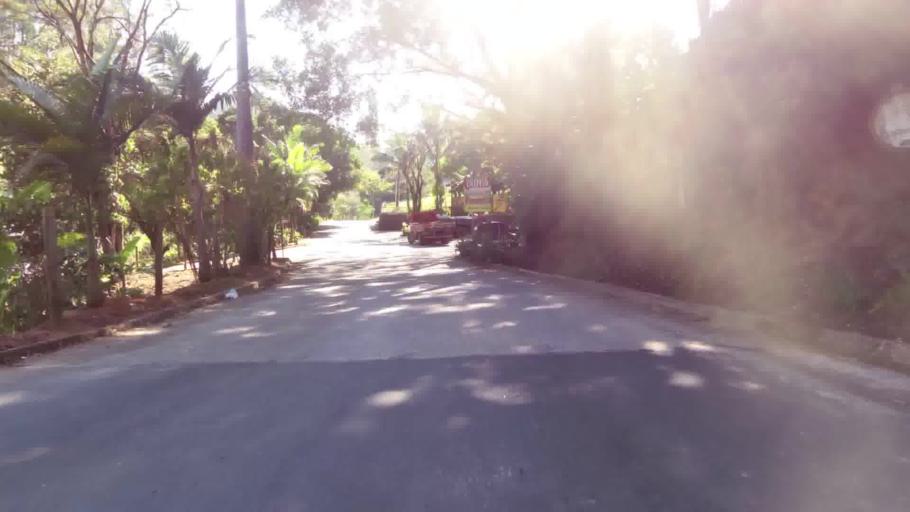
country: BR
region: Espirito Santo
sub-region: Alfredo Chaves
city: Alfredo Chaves
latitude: -20.5885
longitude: -40.7897
